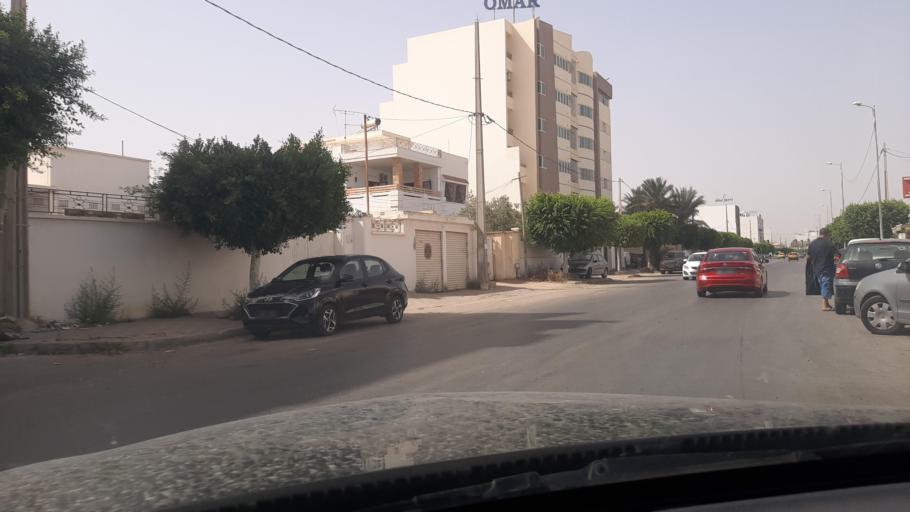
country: TN
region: Safaqis
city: Sfax
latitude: 34.7586
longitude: 10.7560
